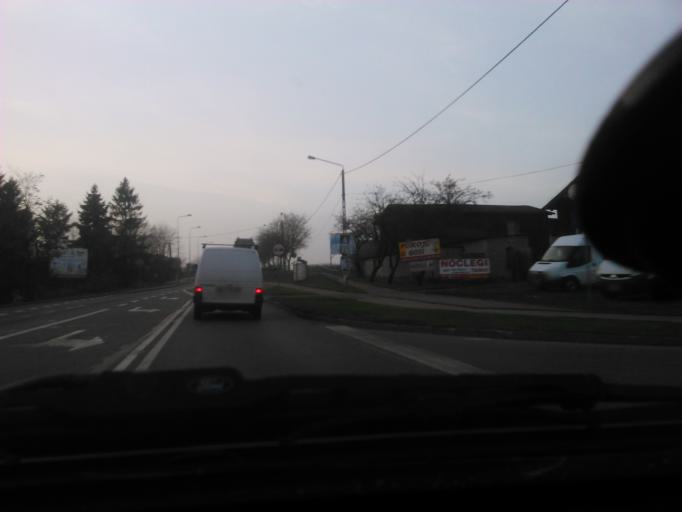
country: PL
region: Pomeranian Voivodeship
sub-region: Powiat kartuski
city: Przodkowo
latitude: 54.3153
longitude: 18.2778
